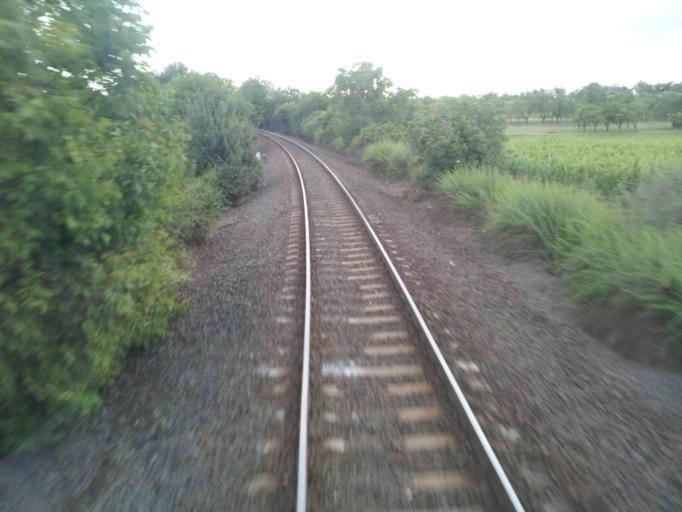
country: HU
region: Veszprem
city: Balatonfured
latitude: 46.9352
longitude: 17.8500
